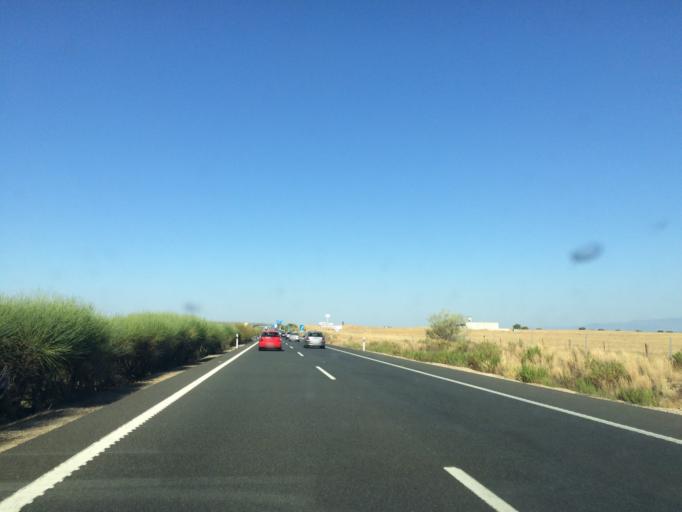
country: ES
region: Extremadura
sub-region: Provincia de Caceres
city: Peraleda de la Mata
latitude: 39.8913
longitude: -5.4134
